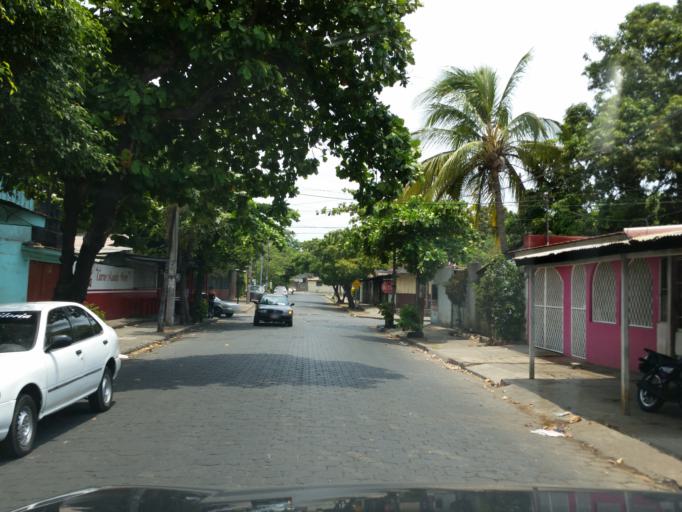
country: NI
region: Managua
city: Managua
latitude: 12.1361
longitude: -86.2415
